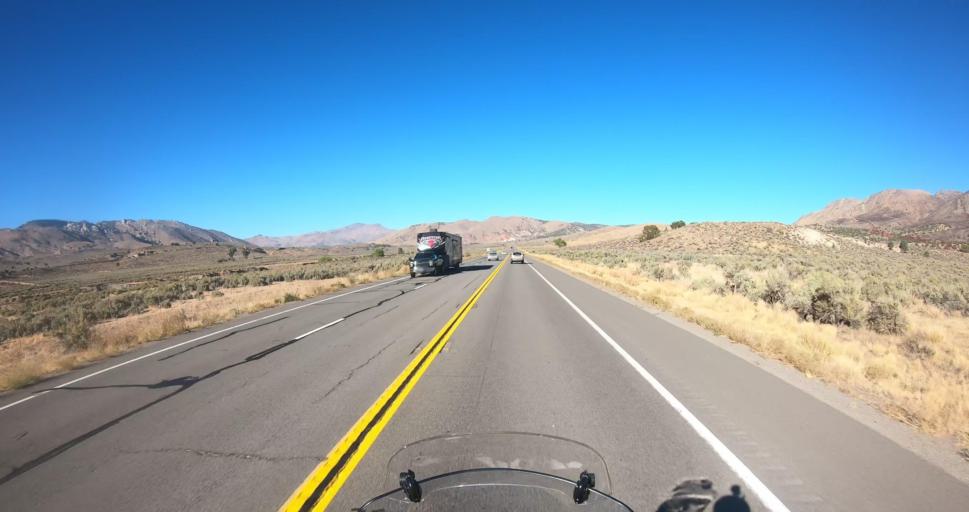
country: US
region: Nevada
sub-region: Washoe County
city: Cold Springs
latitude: 39.8752
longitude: -120.0327
